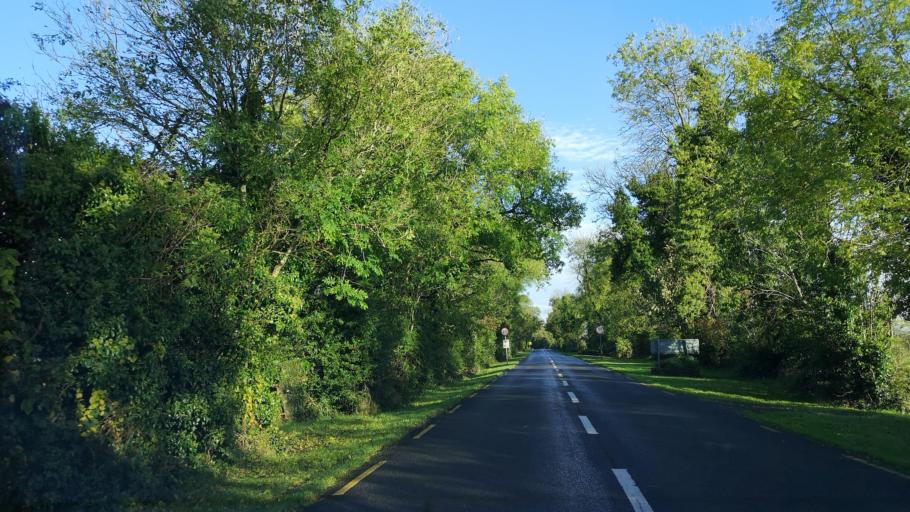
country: IE
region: Connaught
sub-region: Roscommon
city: Castlerea
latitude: 53.8215
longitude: -8.5545
